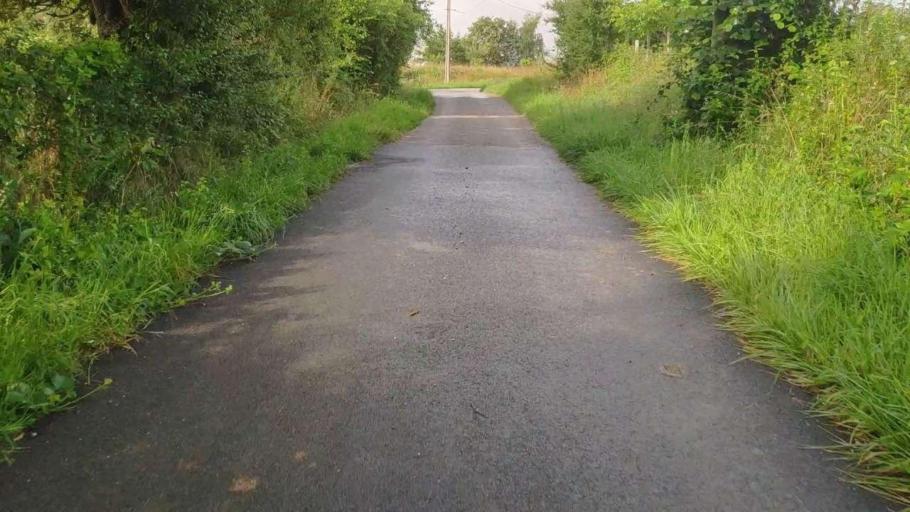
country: FR
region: Franche-Comte
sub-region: Departement du Jura
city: Mont-sous-Vaudrey
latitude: 46.8747
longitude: 5.5282
